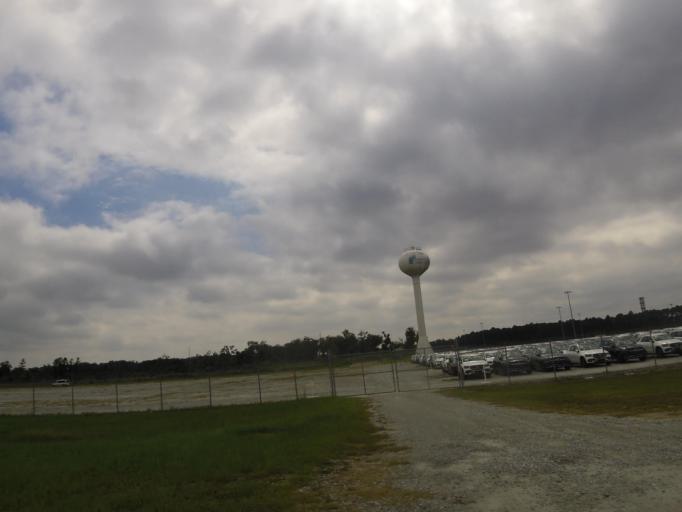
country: US
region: Georgia
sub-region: Glynn County
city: Brunswick
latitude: 31.1087
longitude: -81.5398
